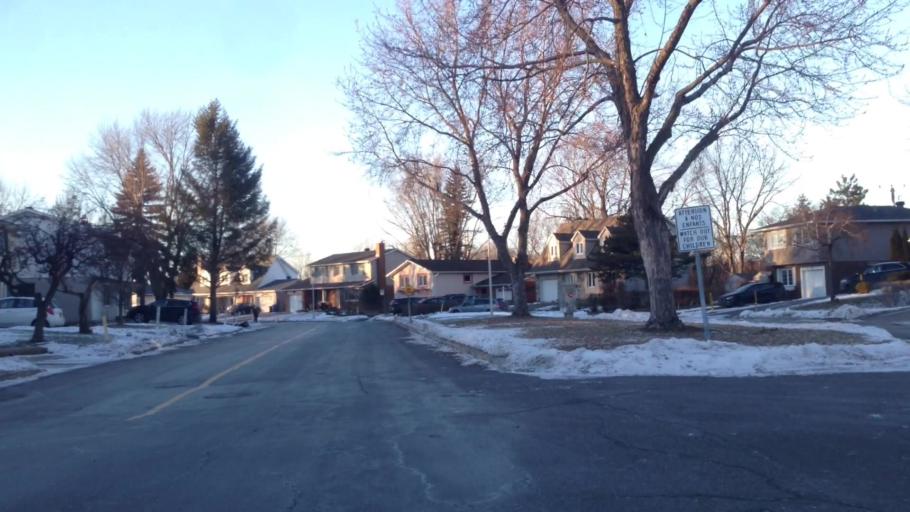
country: CA
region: Quebec
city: Dollard-Des Ormeaux
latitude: 45.4801
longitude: -73.8441
